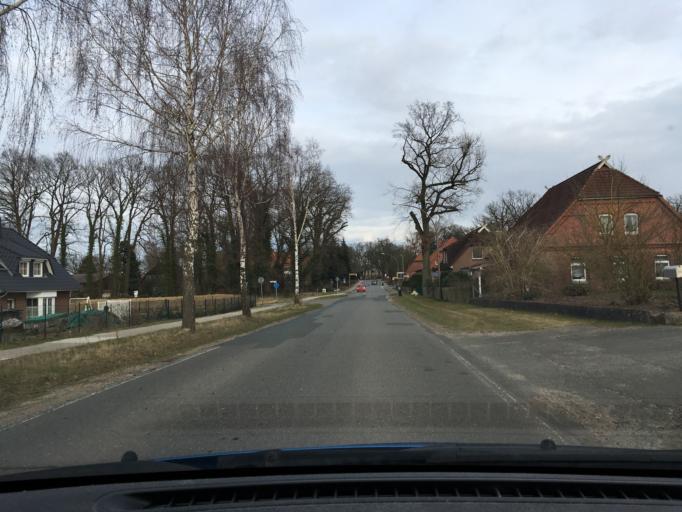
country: DE
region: Lower Saxony
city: Vogelsen
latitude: 53.2787
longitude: 10.3456
